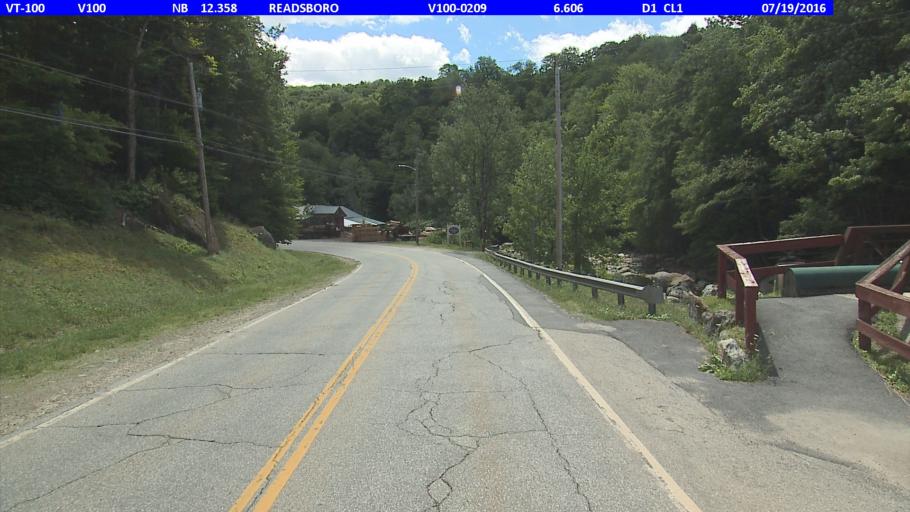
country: US
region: Massachusetts
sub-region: Franklin County
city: Charlemont
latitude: 42.7759
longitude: -72.9525
